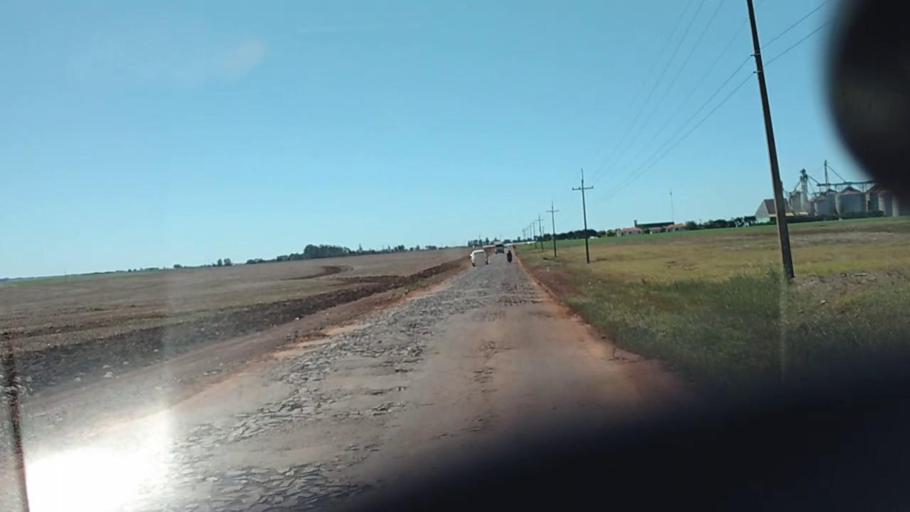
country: PY
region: Alto Parana
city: Naranjal
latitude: -25.9736
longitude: -55.1550
